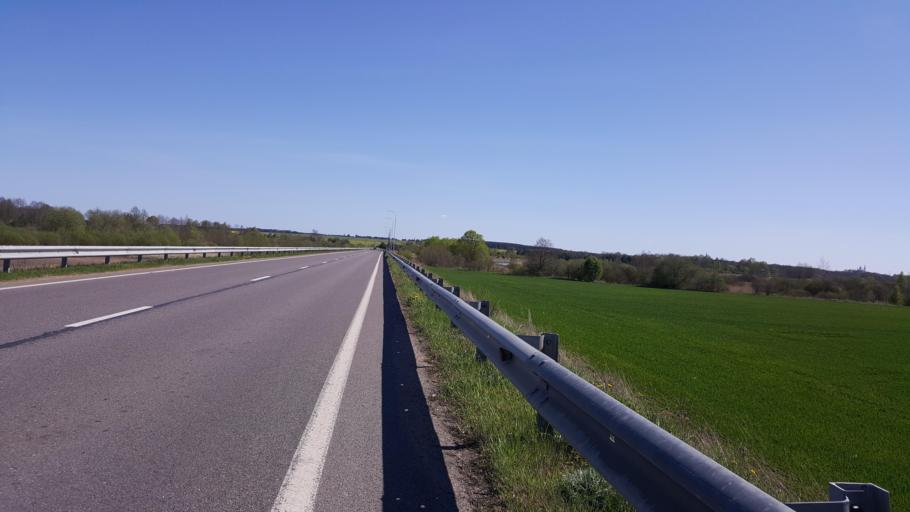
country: BY
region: Brest
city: Kamyanyets
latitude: 52.4312
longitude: 23.8345
